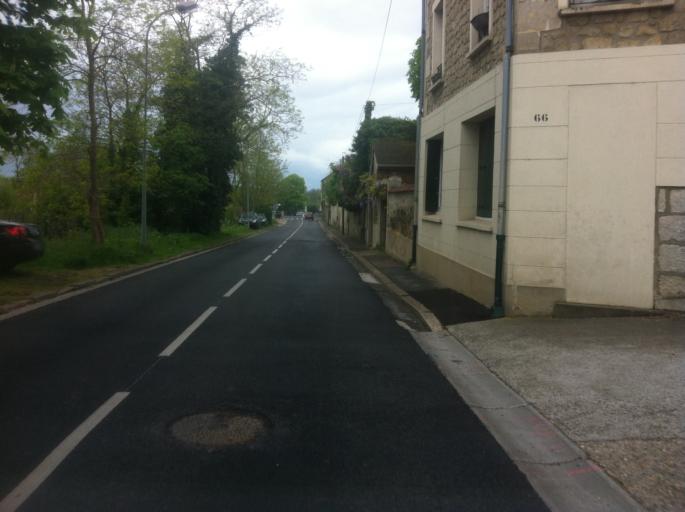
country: FR
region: Ile-de-France
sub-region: Departement du Val-d'Oise
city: Auvers-sur-Oise
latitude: 49.0718
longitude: 2.1791
